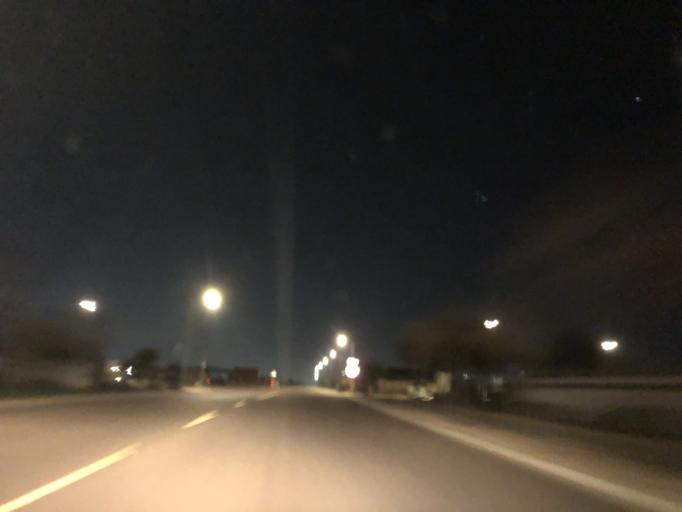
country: US
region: Arizona
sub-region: Maricopa County
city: Tolleson
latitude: 33.4101
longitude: -112.2734
